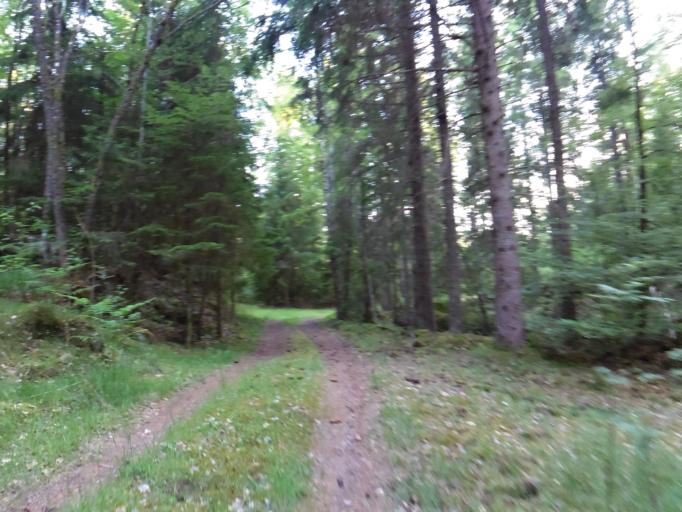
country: SE
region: Blekinge
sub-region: Olofstroms Kommun
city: Olofstroem
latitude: 56.4166
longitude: 14.5496
